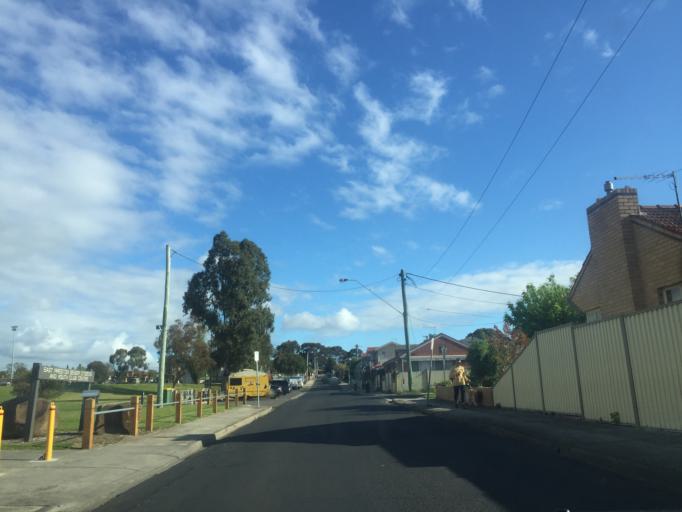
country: AU
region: Victoria
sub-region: Darebin
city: Preston
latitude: -37.7324
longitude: 145.0227
